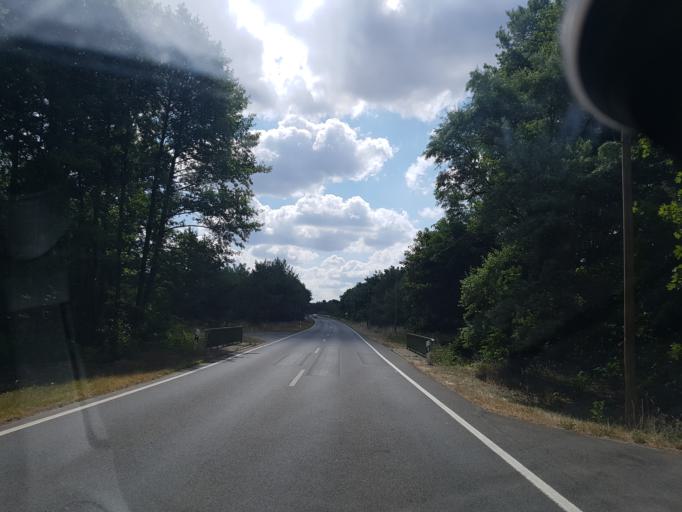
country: DE
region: Brandenburg
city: Drebkau
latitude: 51.6720
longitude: 14.1707
